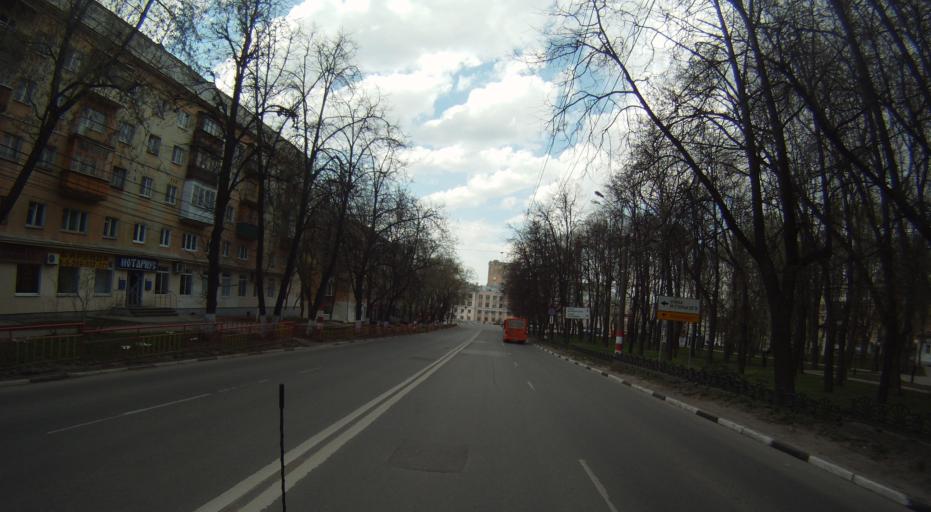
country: RU
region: Nizjnij Novgorod
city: Nizhniy Novgorod
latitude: 56.3166
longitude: 44.0154
